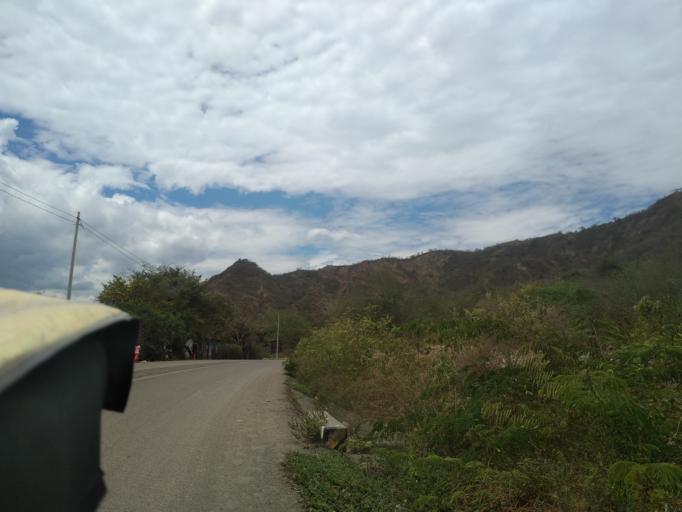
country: PE
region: Cajamarca
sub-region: Provincia de San Ignacio
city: La Coipa
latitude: -5.3687
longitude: -78.7856
